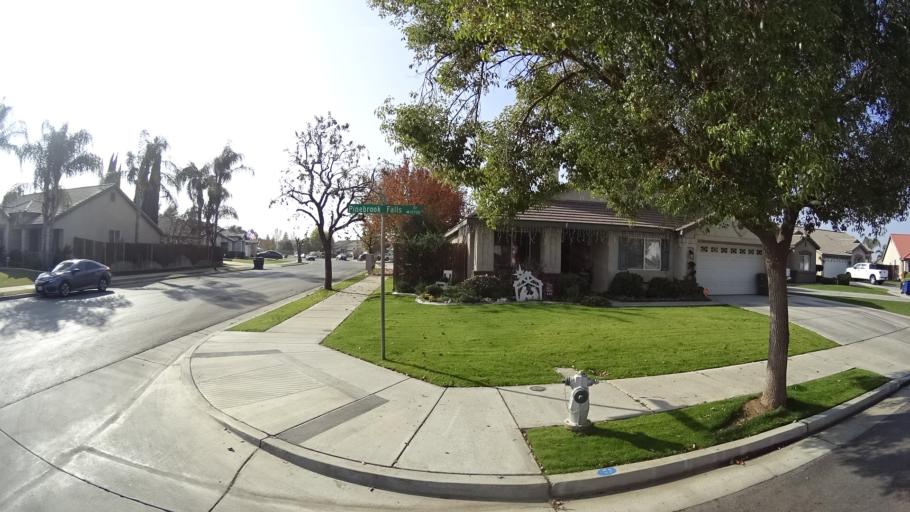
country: US
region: California
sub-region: Kern County
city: Greenacres
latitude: 35.4149
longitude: -119.1209
